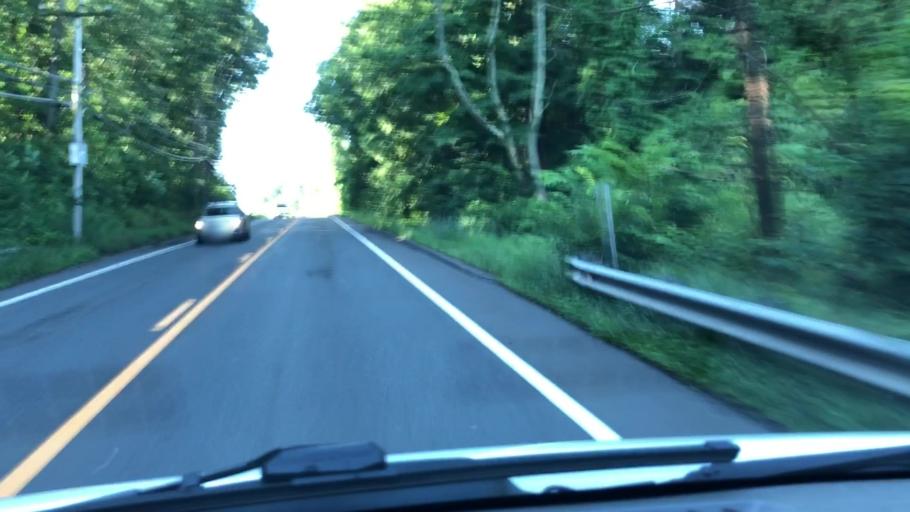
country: US
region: Massachusetts
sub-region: Franklin County
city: South Deerfield
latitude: 42.5138
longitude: -72.6057
